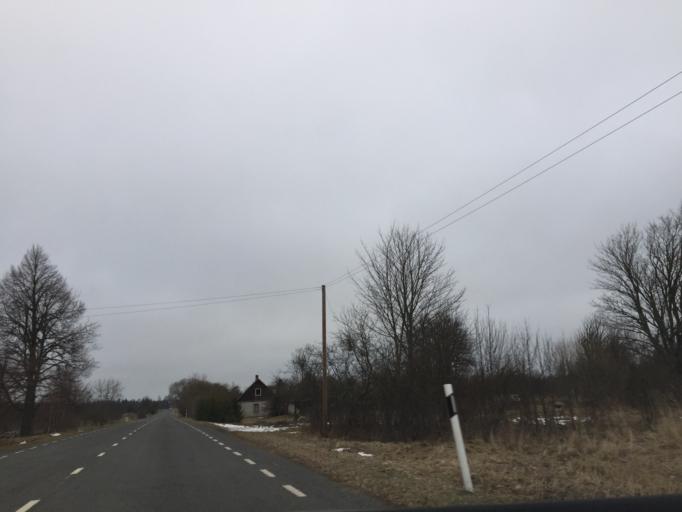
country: EE
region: Saare
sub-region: Kuressaare linn
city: Kuressaare
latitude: 58.5322
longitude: 22.3411
